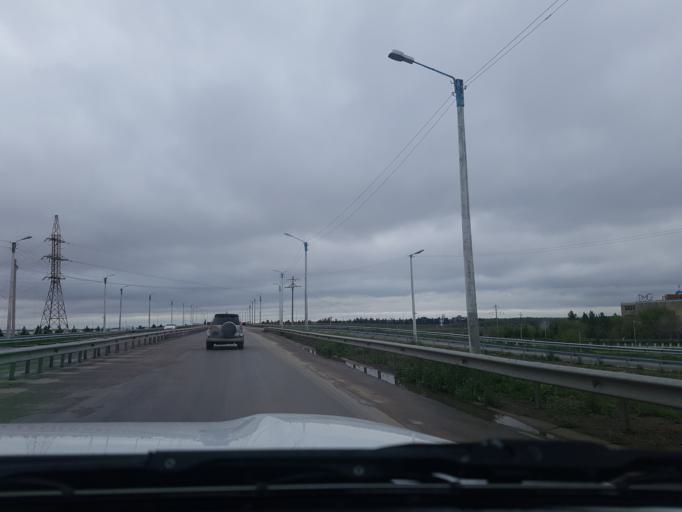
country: TM
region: Mary
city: Mary
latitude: 37.5945
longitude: 61.8859
